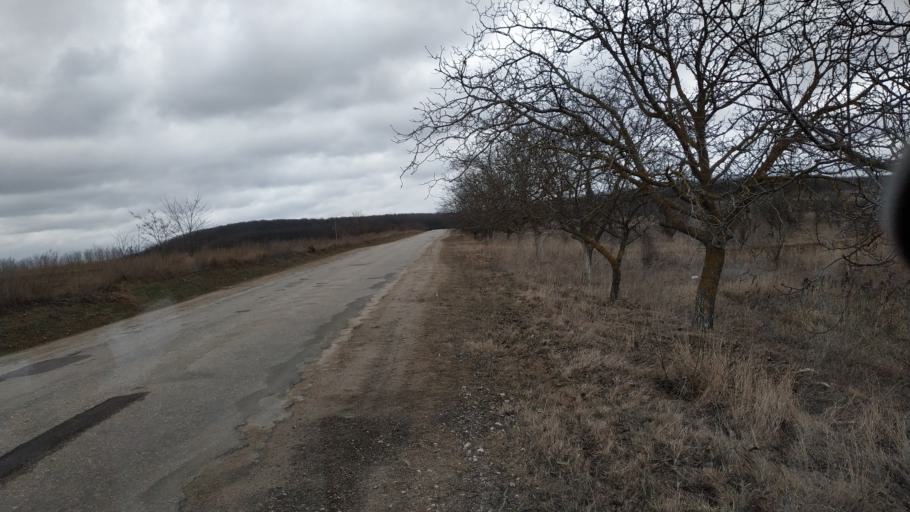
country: MD
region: Calarasi
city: Calarasi
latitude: 47.2215
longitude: 28.2649
